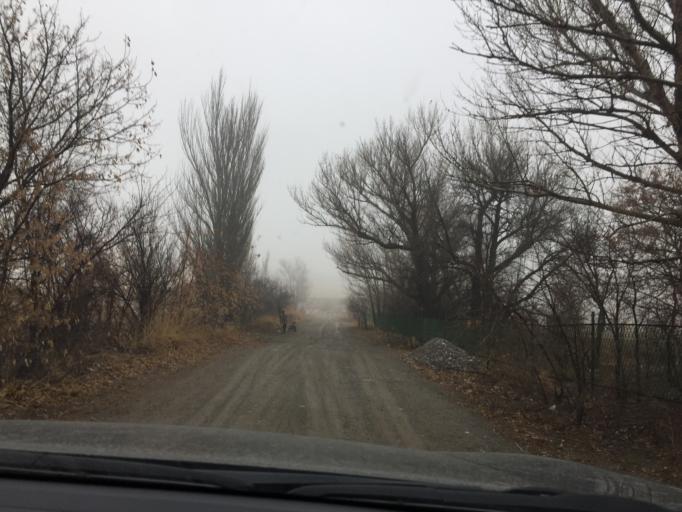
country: KZ
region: Ongtustik Qazaqstan
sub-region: Tulkibas Audany
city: Zhabagly
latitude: 42.5138
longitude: 70.5625
